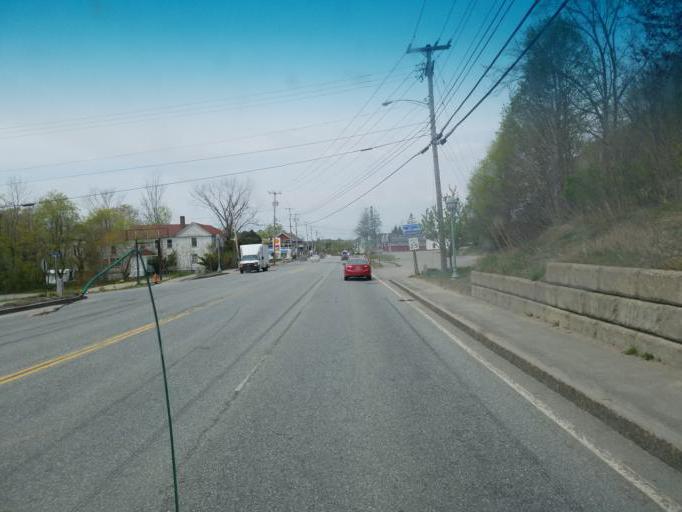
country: US
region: Maine
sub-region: Hancock County
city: Ellsworth
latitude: 44.5400
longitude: -68.4166
